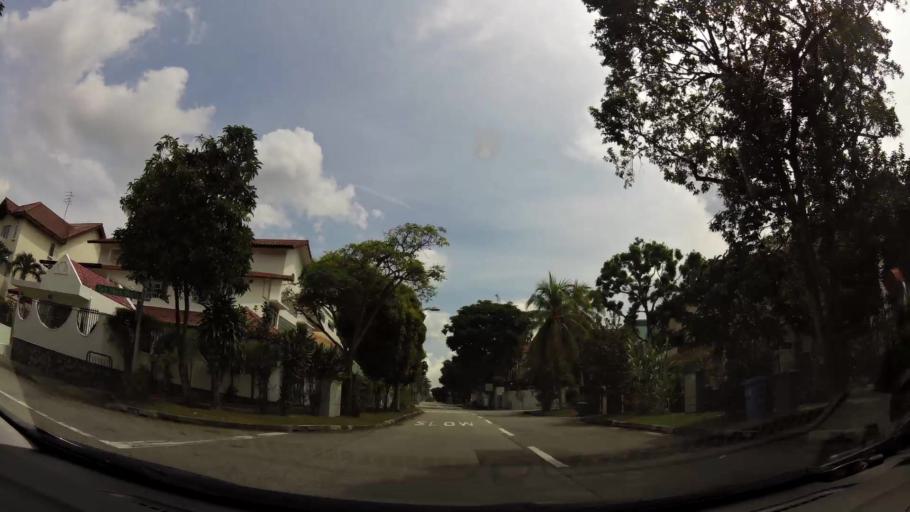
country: SG
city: Singapore
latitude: 1.3369
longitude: 103.7660
